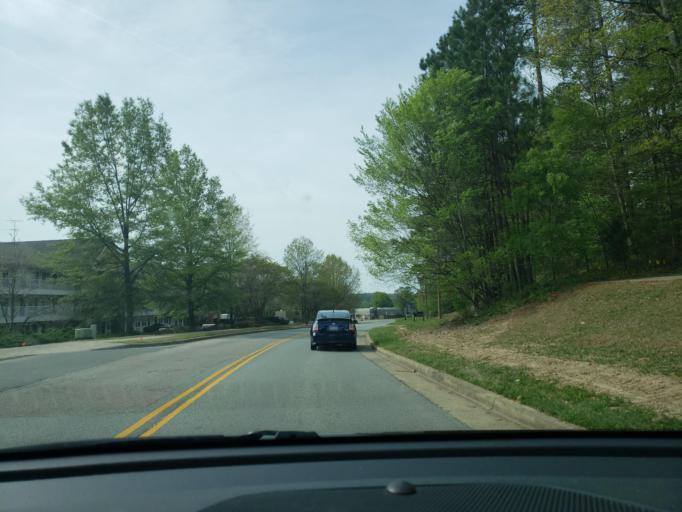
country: US
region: North Carolina
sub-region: Durham County
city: Durham
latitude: 35.9727
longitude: -78.9579
